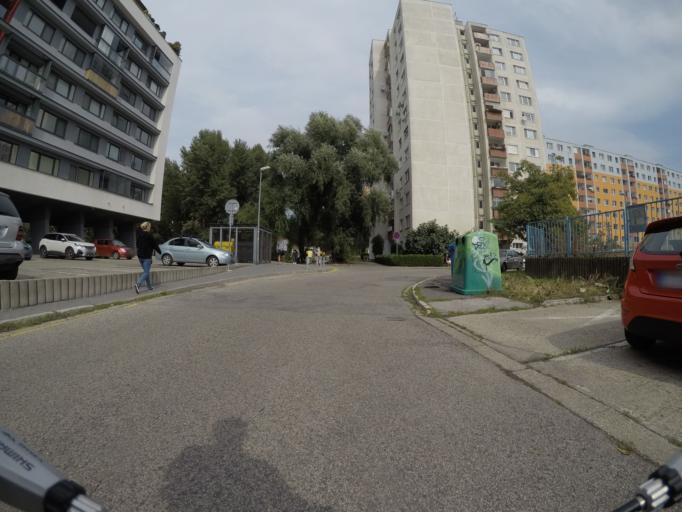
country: SK
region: Bratislavsky
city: Bratislava
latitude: 48.1538
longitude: 17.1566
